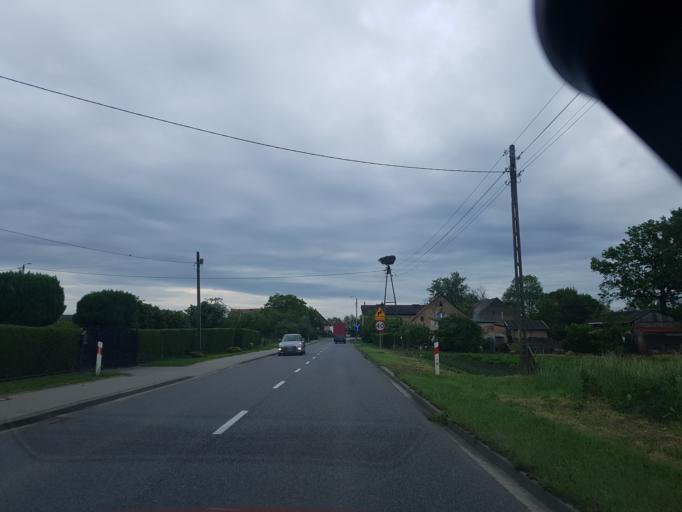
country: PL
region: Lower Silesian Voivodeship
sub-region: Powiat wroclawski
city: Gniechowice
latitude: 50.9835
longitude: 16.8460
